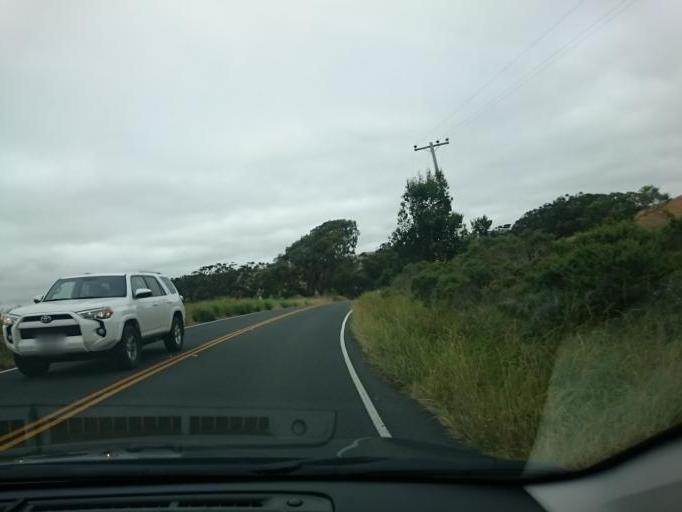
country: US
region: California
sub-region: Marin County
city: Inverness
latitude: 38.1238
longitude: -122.8571
